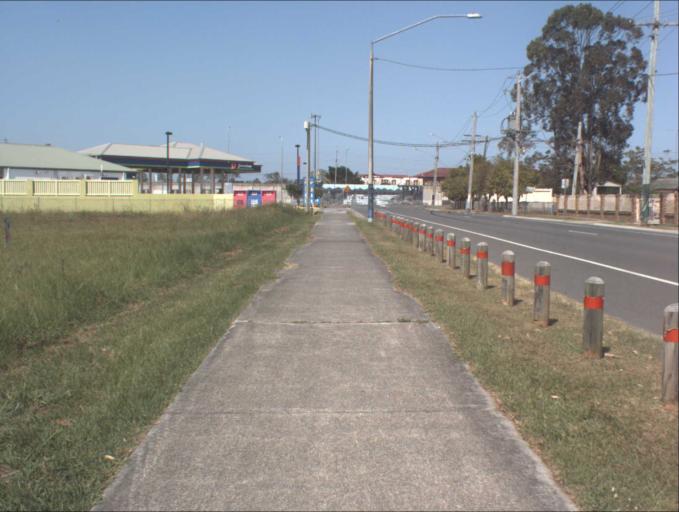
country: AU
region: Queensland
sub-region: Logan
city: Beenleigh
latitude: -27.6901
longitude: 153.1897
